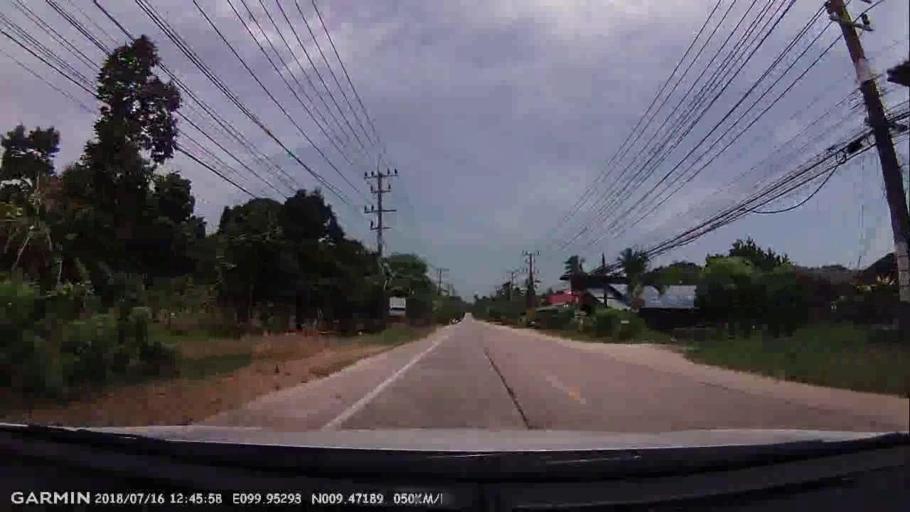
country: TH
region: Surat Thani
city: Ko Samui
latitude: 9.4718
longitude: 99.9529
